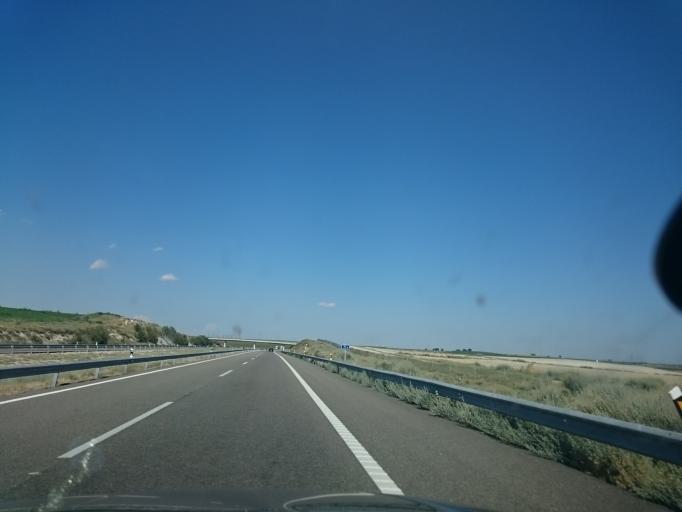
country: ES
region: Aragon
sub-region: Provincia de Zaragoza
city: Bujaraloz
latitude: 41.5178
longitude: -0.1236
